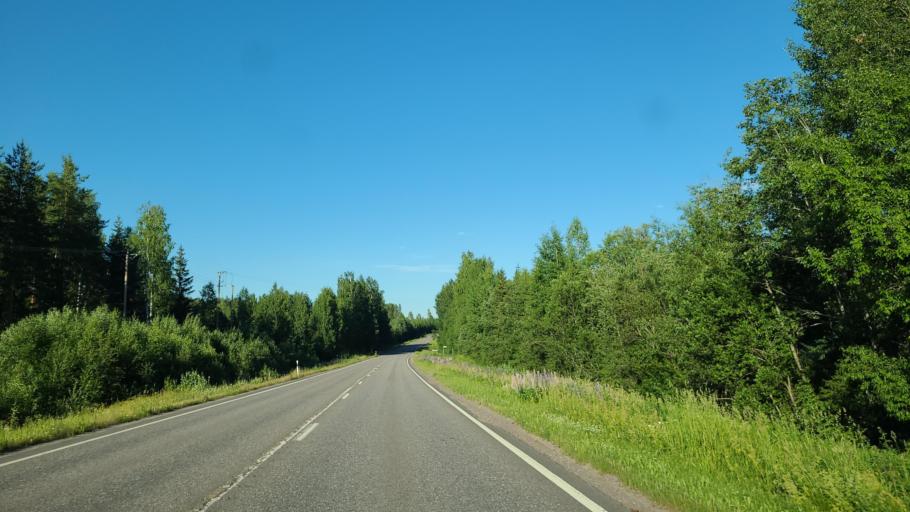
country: FI
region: Northern Savo
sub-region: Varkaus
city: Varkaus
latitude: 62.2960
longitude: 27.7916
